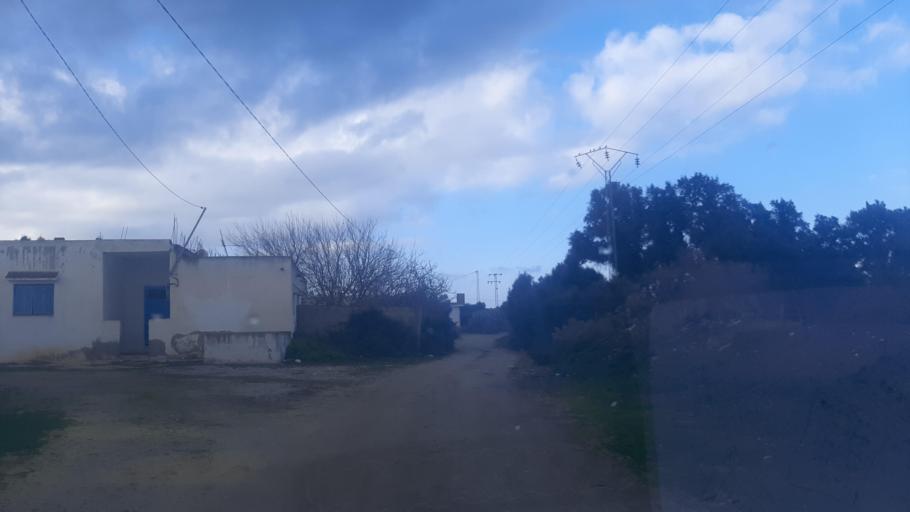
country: TN
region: Nabul
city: Manzil Bu Zalafah
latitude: 36.7428
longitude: 10.5272
